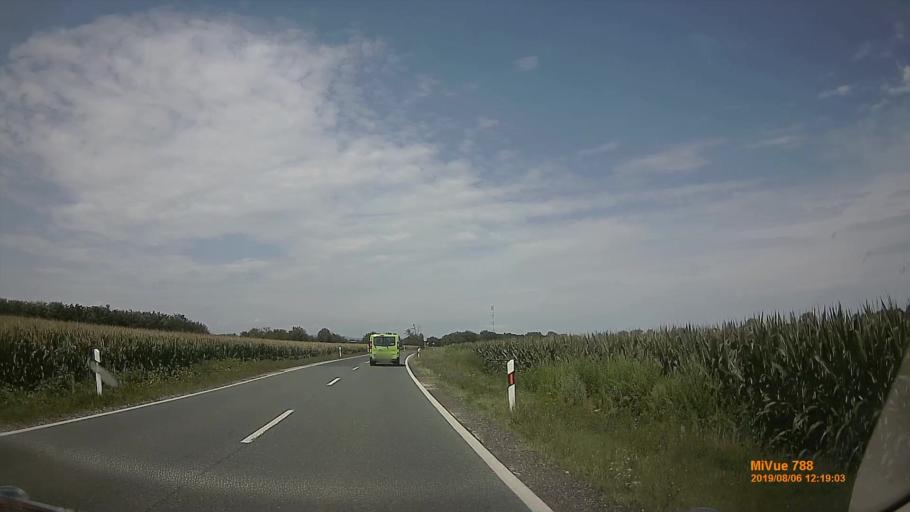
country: HU
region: Vas
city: Vep
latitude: 47.1734
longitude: 16.7665
